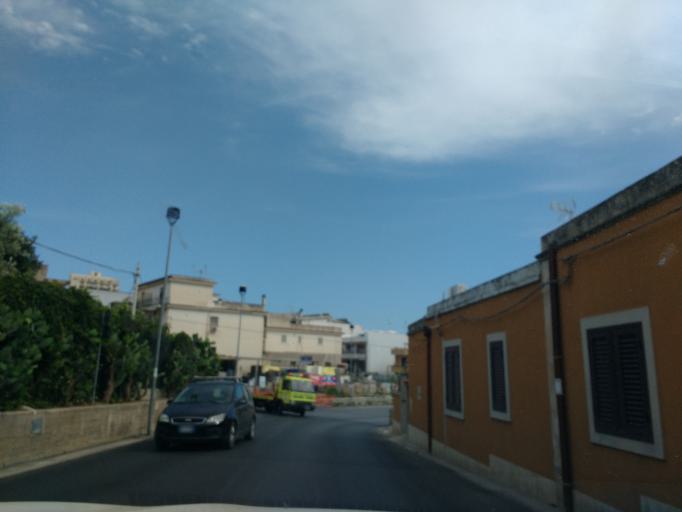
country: IT
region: Sicily
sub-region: Provincia di Siracusa
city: Noto
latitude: 36.8895
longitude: 15.0626
